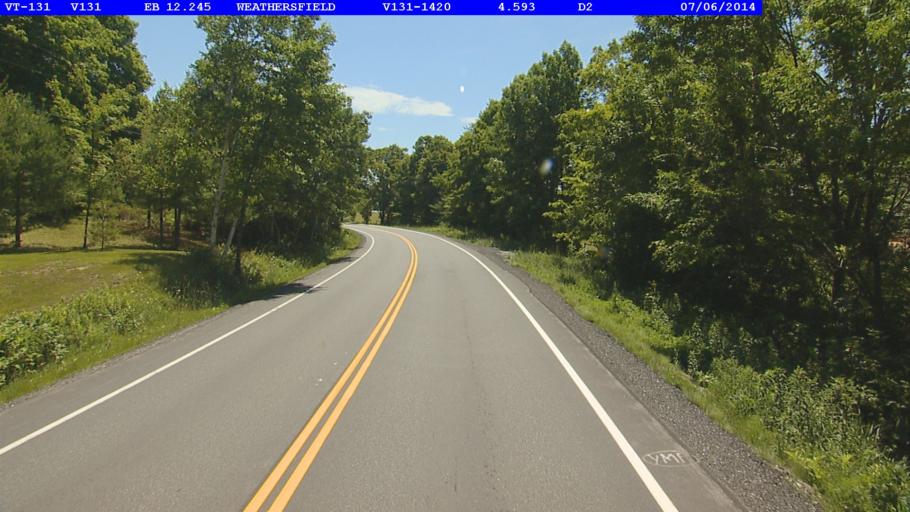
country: US
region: Vermont
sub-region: Windsor County
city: Windsor
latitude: 43.4243
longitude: -72.4757
